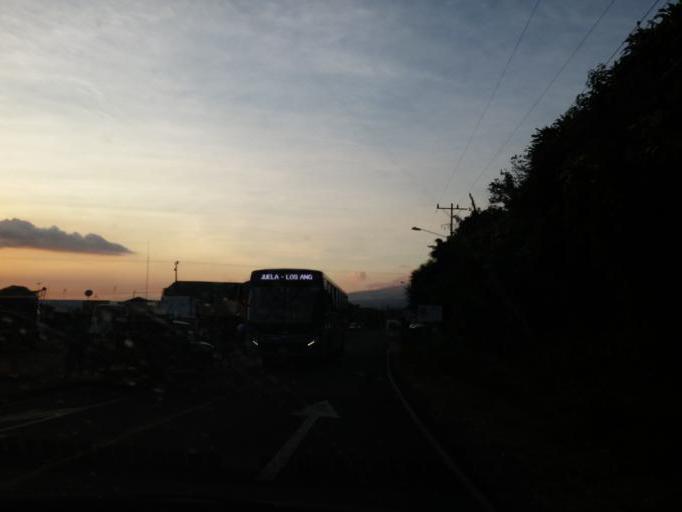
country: CR
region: Alajuela
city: Sabanilla
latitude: 10.0755
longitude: -84.2148
